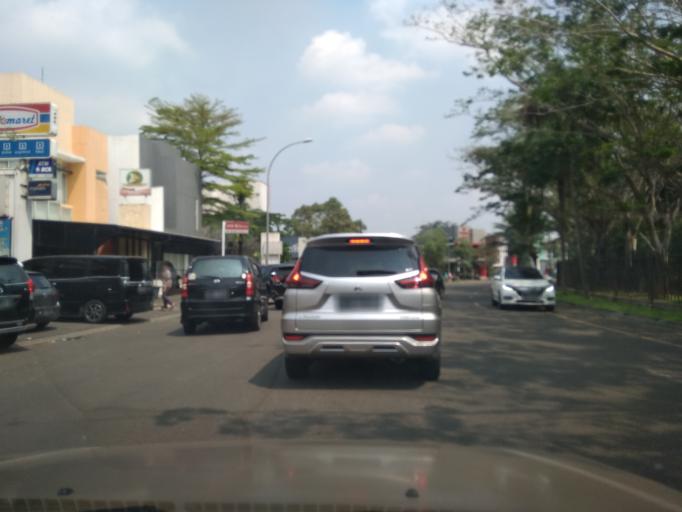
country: ID
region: West Java
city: Serpong
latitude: -6.3150
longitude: 106.6473
